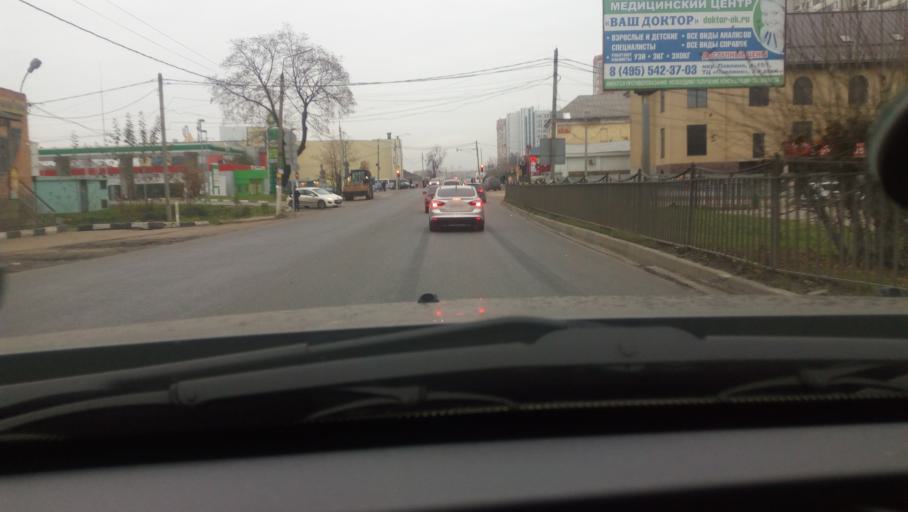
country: RU
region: Moskovskaya
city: Saltykovka
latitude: 55.7513
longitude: 37.9525
